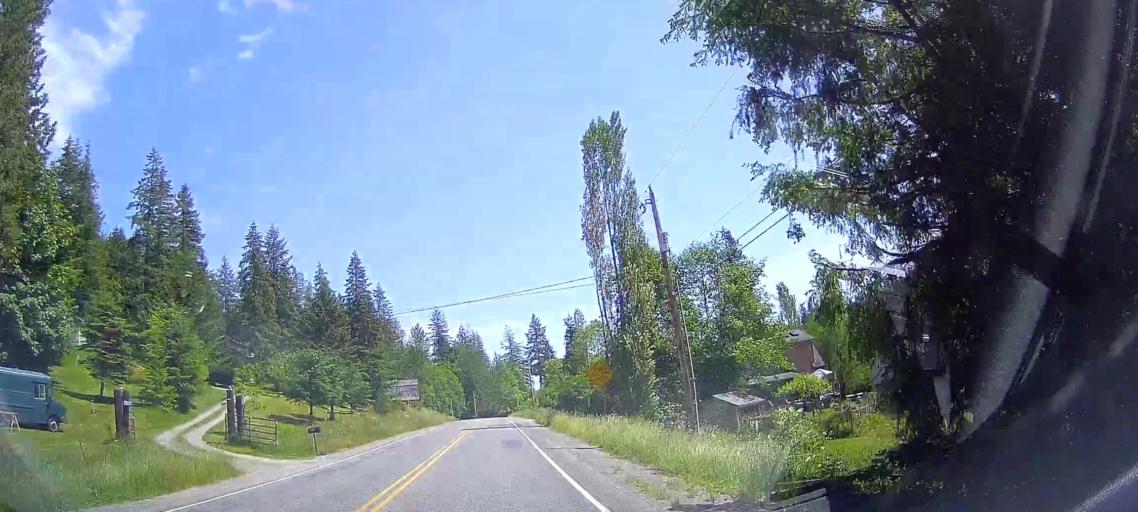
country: US
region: Washington
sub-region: Skagit County
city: Big Lake
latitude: 48.3945
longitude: -122.2697
